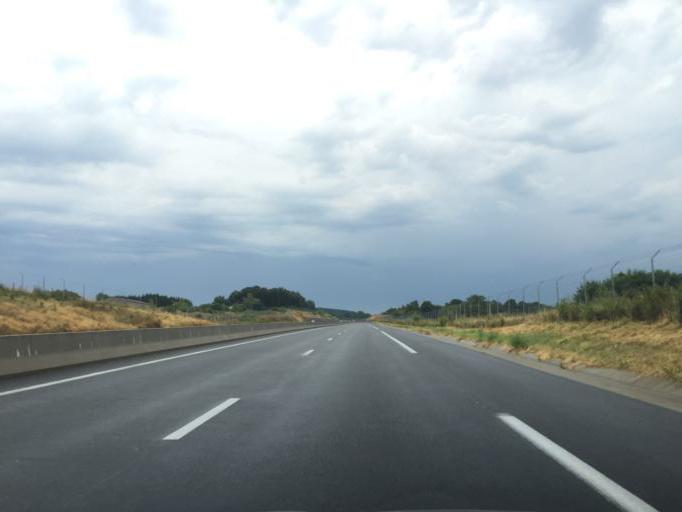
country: FR
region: Auvergne
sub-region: Departement de l'Allier
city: Lapalisse
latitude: 46.2171
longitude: 3.7037
